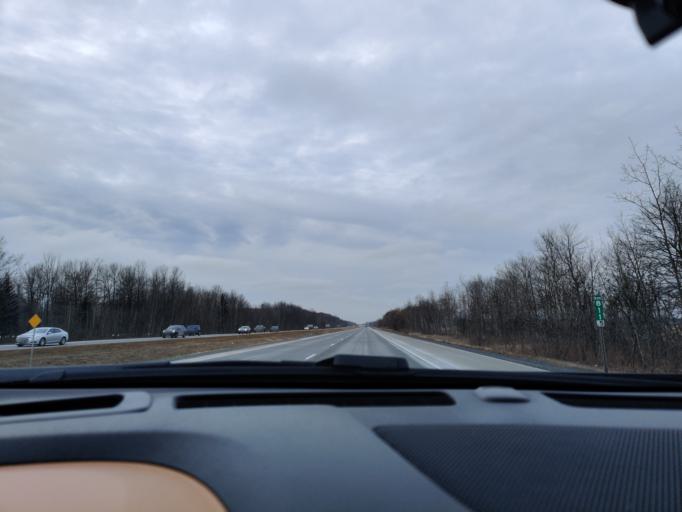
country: CA
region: Ontario
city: Cornwall
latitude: 45.1251
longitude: -74.5215
